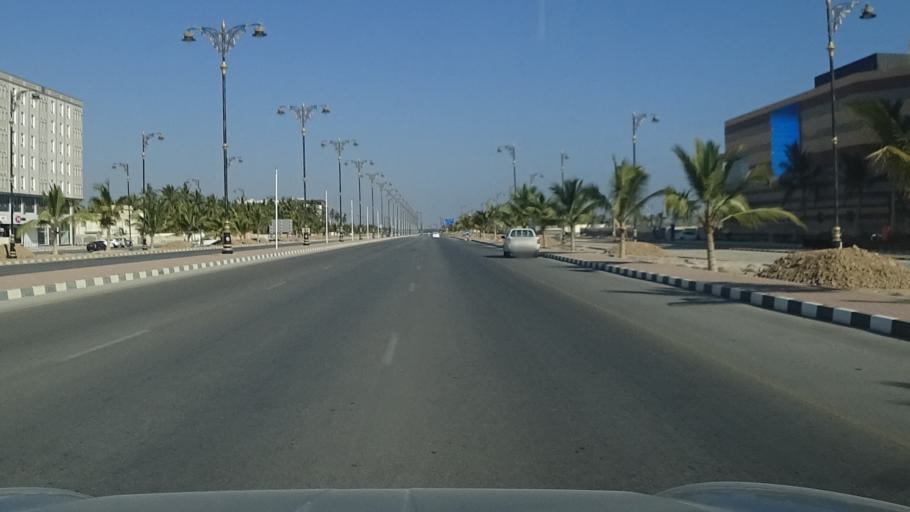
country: OM
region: Zufar
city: Salalah
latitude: 17.0362
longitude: 54.1641
